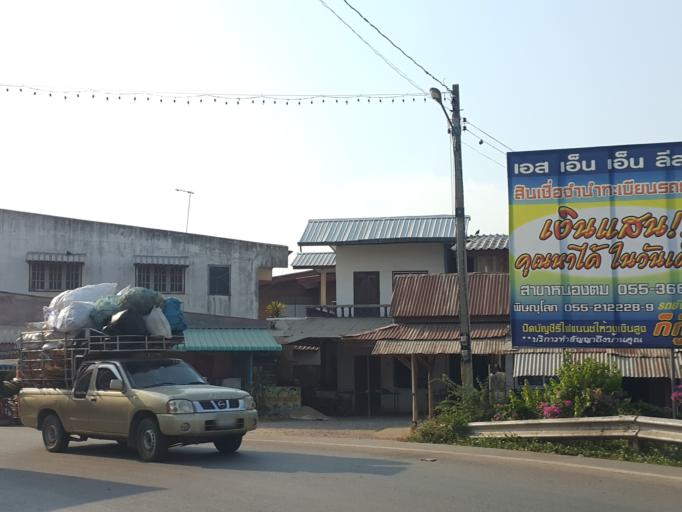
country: TH
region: Phitsanulok
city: Phrom Phiram
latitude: 17.0359
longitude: 100.1987
